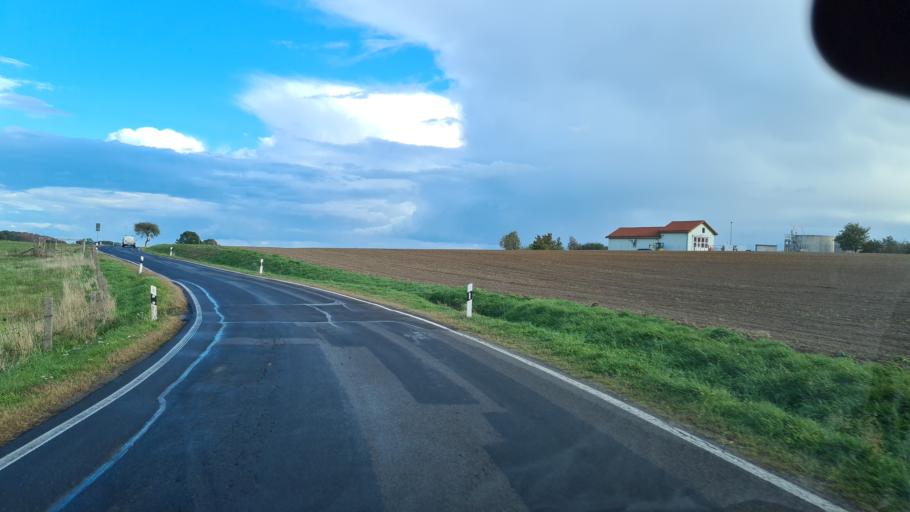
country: DE
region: Saxony
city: Dahlen
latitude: 51.3637
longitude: 13.0148
